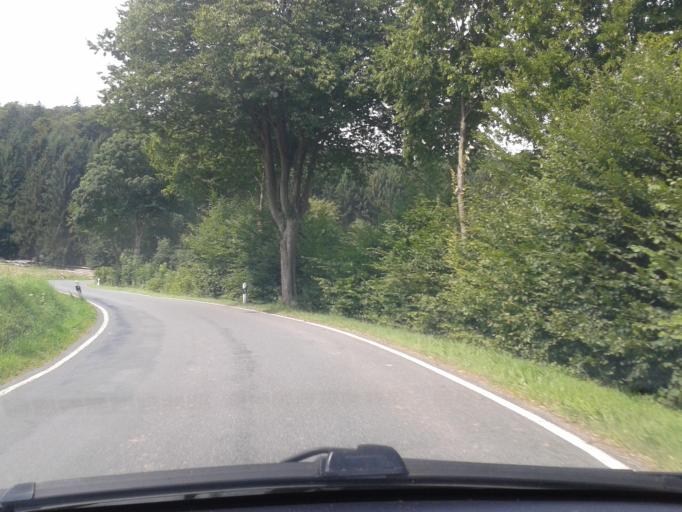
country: DE
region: North Rhine-Westphalia
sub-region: Regierungsbezirk Detmold
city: Lugde
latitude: 51.9548
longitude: 9.1961
